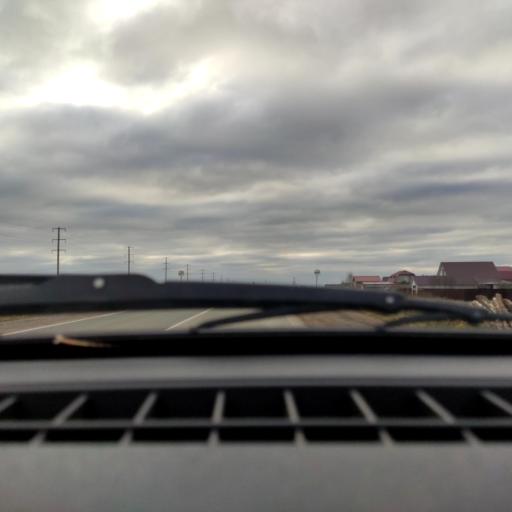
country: RU
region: Bashkortostan
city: Iglino
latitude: 54.7944
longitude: 56.2514
